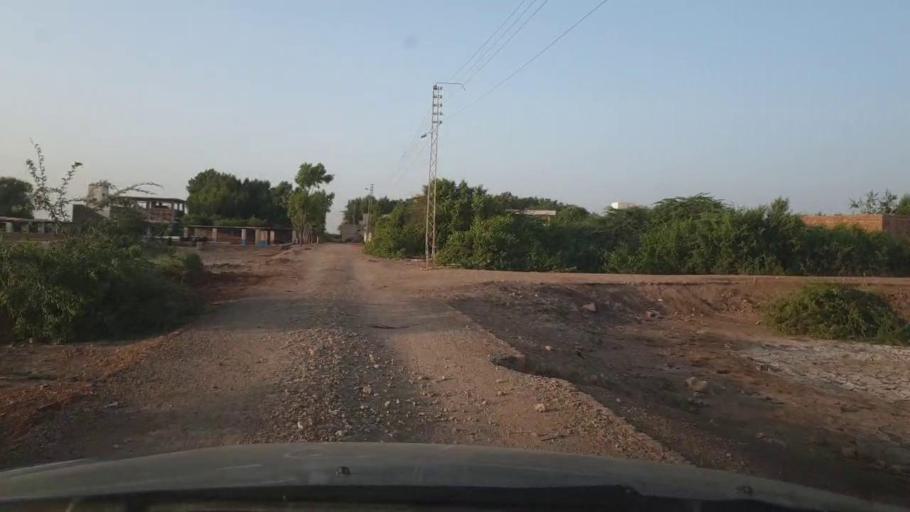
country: PK
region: Sindh
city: Tando Ghulam Ali
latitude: 25.1742
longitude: 68.9749
